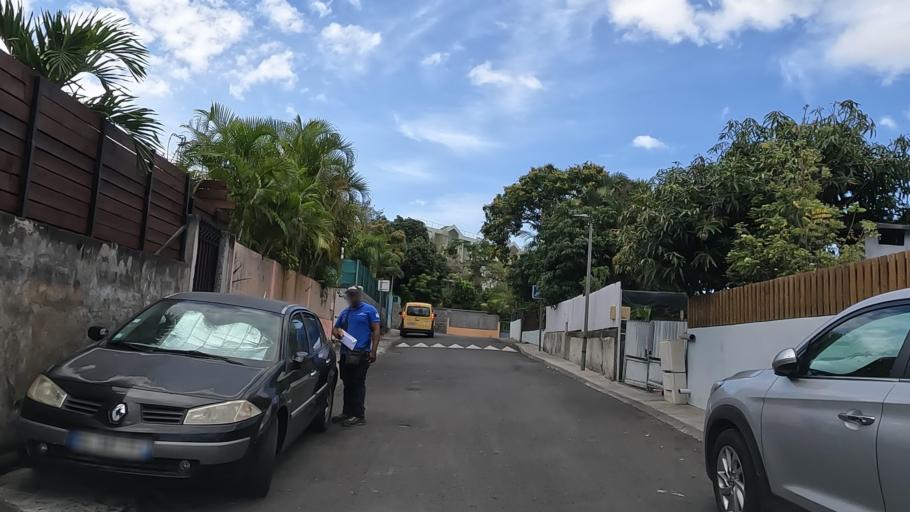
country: RE
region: Reunion
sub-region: Reunion
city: La Possession
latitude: -20.9487
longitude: 55.3304
